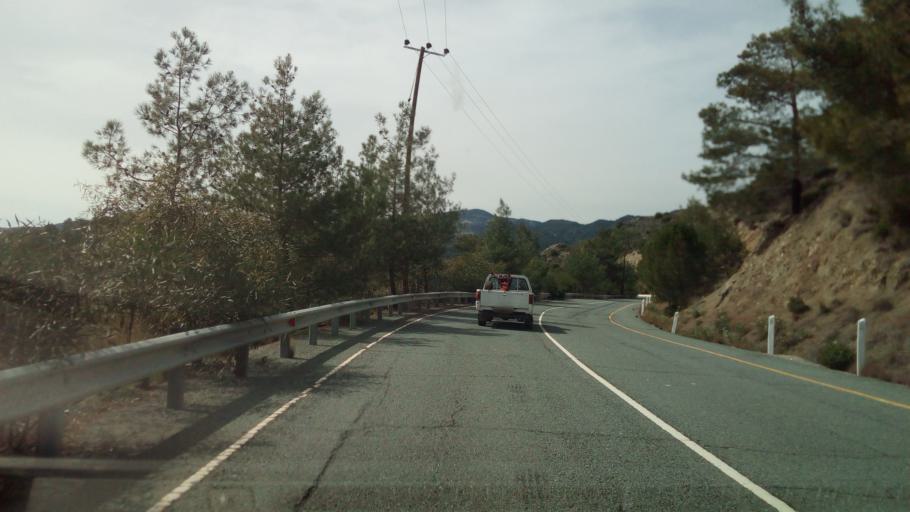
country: CY
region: Limassol
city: Pelendri
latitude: 34.8677
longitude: 32.9302
